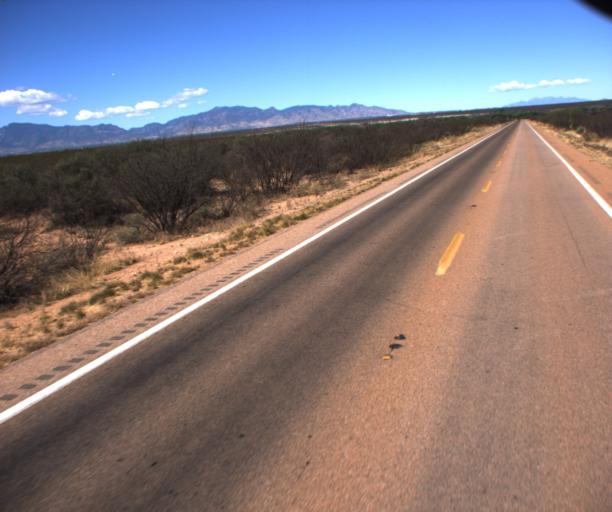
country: US
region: Arizona
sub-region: Cochise County
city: Sierra Vista Southeast
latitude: 31.5524
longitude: -110.1215
